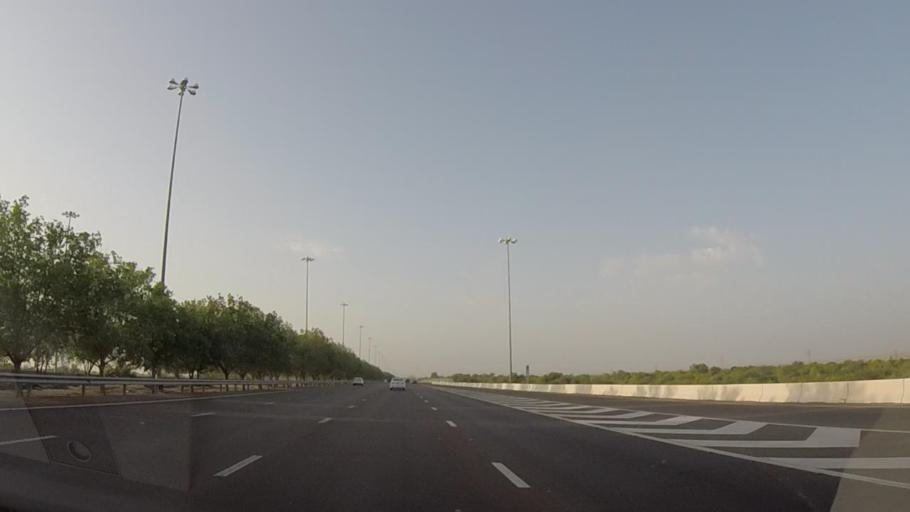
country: AE
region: Dubai
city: Dubai
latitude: 24.7943
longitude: 54.8610
